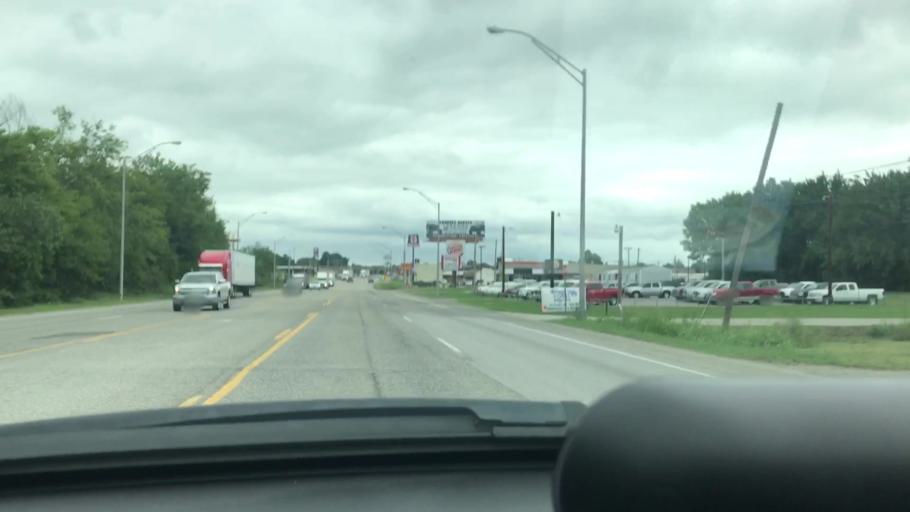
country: US
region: Oklahoma
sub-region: Wagoner County
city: Wagoner
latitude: 35.9542
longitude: -95.3952
